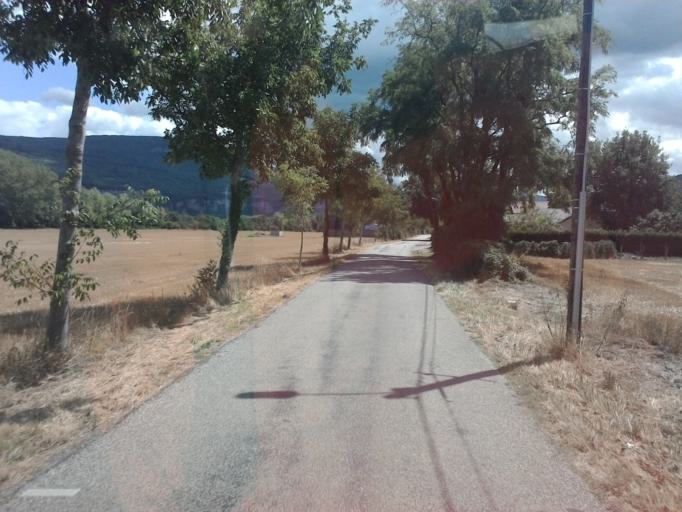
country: FR
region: Rhone-Alpes
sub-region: Departement de l'Ain
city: Saint-Sorlin-en-Bugey
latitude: 45.8792
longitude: 5.3553
